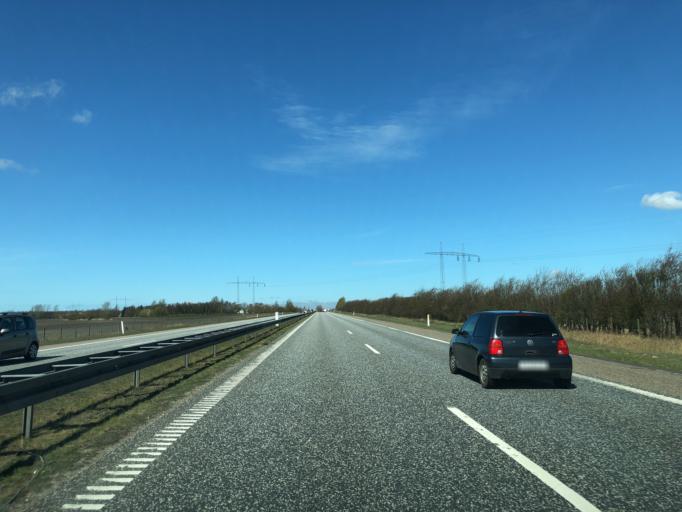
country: DK
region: North Denmark
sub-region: Alborg Kommune
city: Vestbjerg
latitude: 57.1095
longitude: 9.9550
